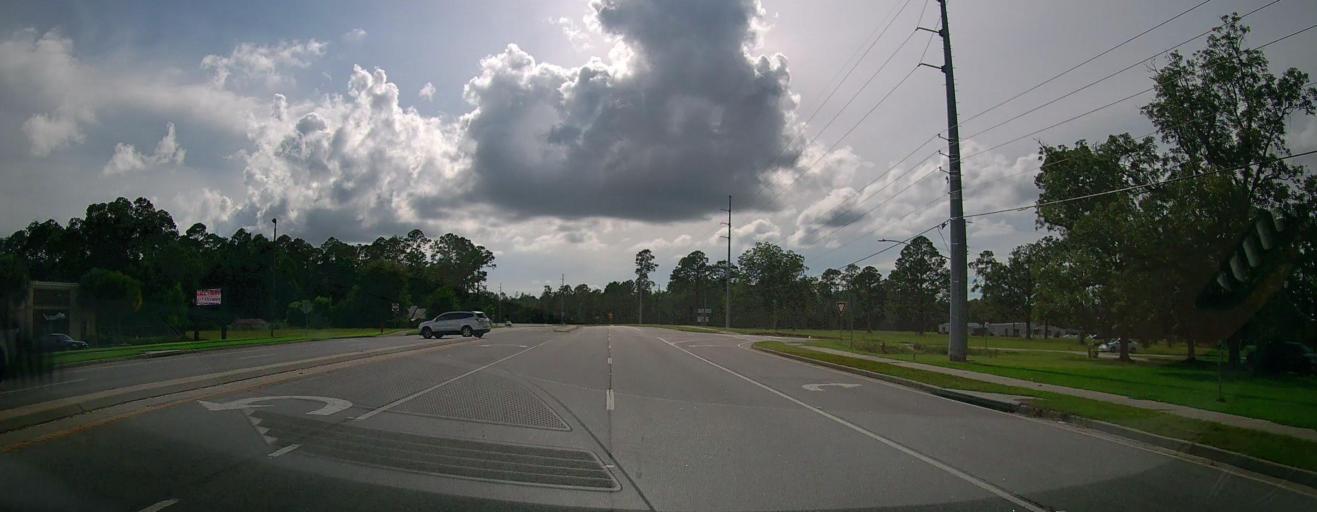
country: US
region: Georgia
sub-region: Wayne County
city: Jesup
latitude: 31.6051
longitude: -81.9151
